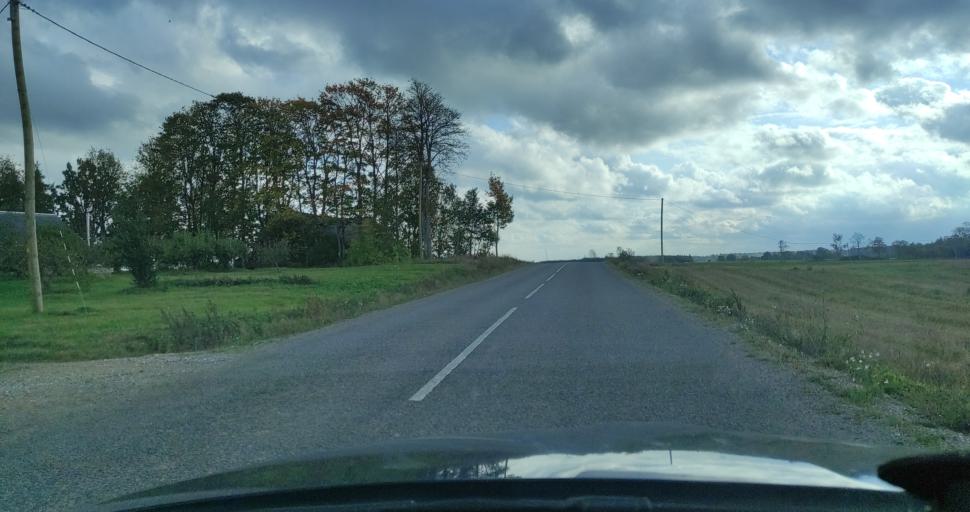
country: LV
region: Talsu Rajons
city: Sabile
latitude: 56.9359
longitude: 22.3968
